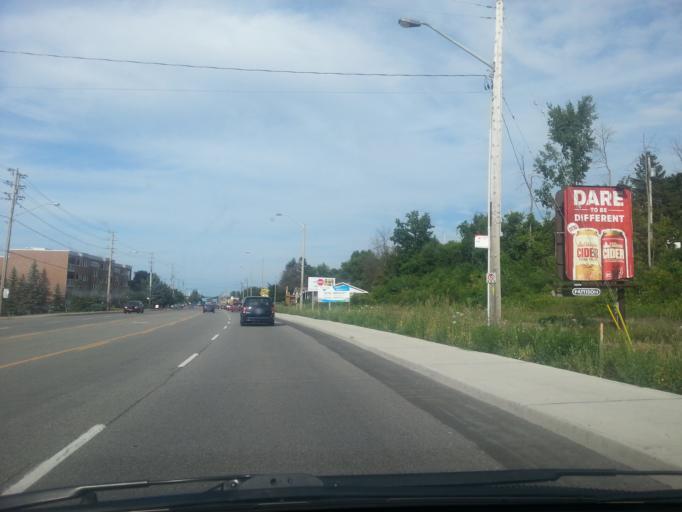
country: CA
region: Quebec
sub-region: Outaouais
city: Gatineau
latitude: 45.4623
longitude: -75.5440
